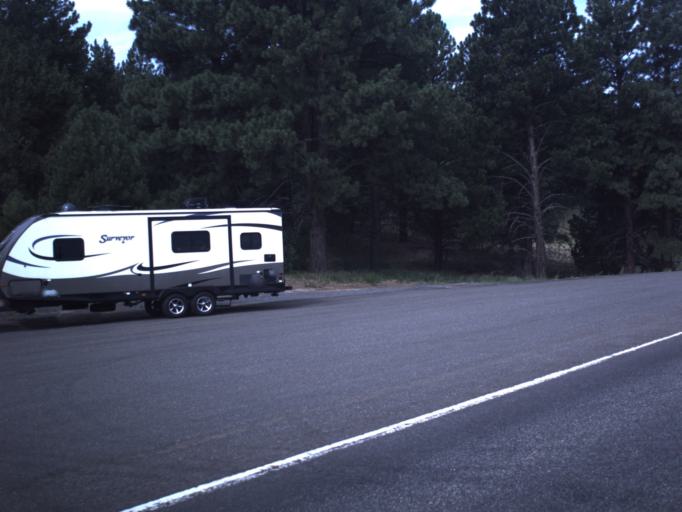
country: US
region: Utah
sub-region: Garfield County
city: Panguitch
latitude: 37.4903
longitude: -112.5200
